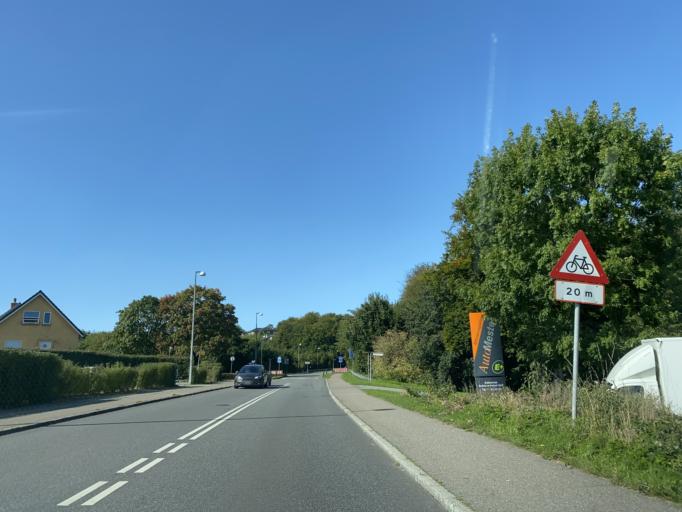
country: DK
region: South Denmark
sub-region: Aabenraa Kommune
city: Aabenraa
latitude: 55.0555
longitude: 9.3948
